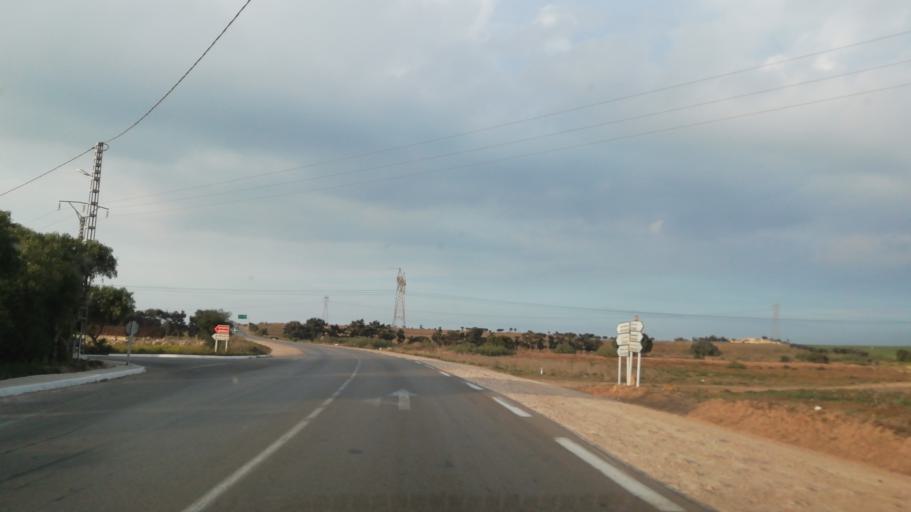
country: DZ
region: Oran
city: Ain el Bya
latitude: 35.7798
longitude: -0.0976
